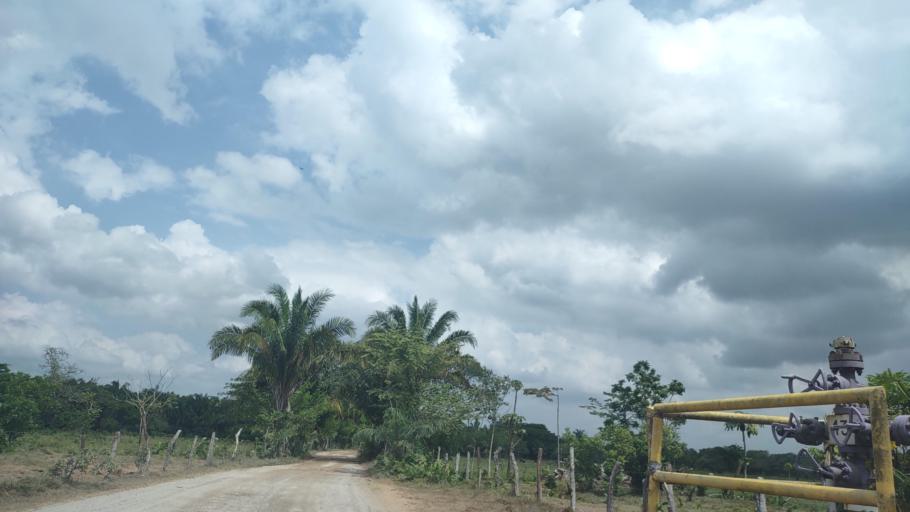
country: MX
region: Veracruz
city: Las Choapas
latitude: 17.9620
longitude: -94.1225
